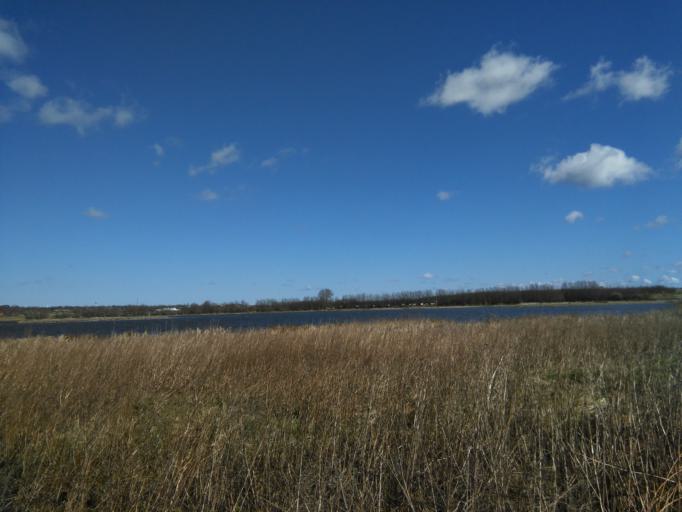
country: DK
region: Central Jutland
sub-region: Arhus Kommune
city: Lystrup
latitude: 56.2125
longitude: 10.2264
